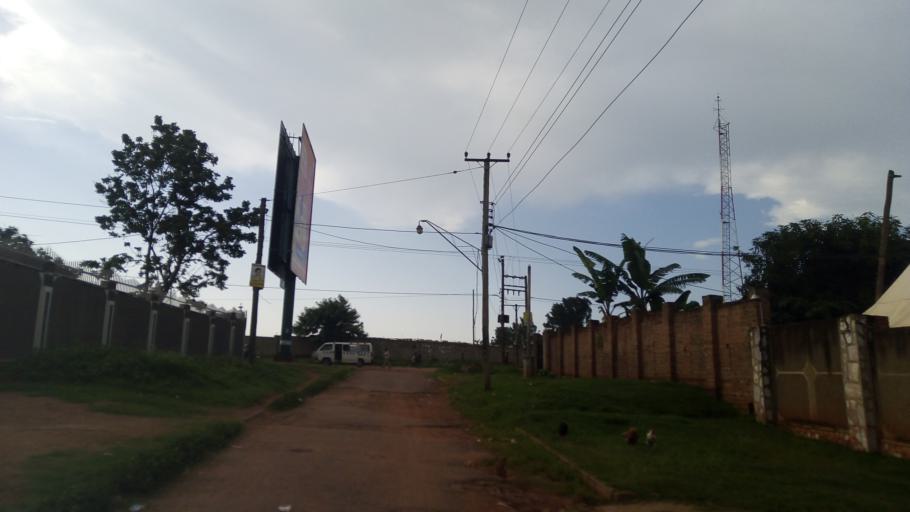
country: UG
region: Eastern Region
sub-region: Mbale District
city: Mbale
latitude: 1.0788
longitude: 34.1683
